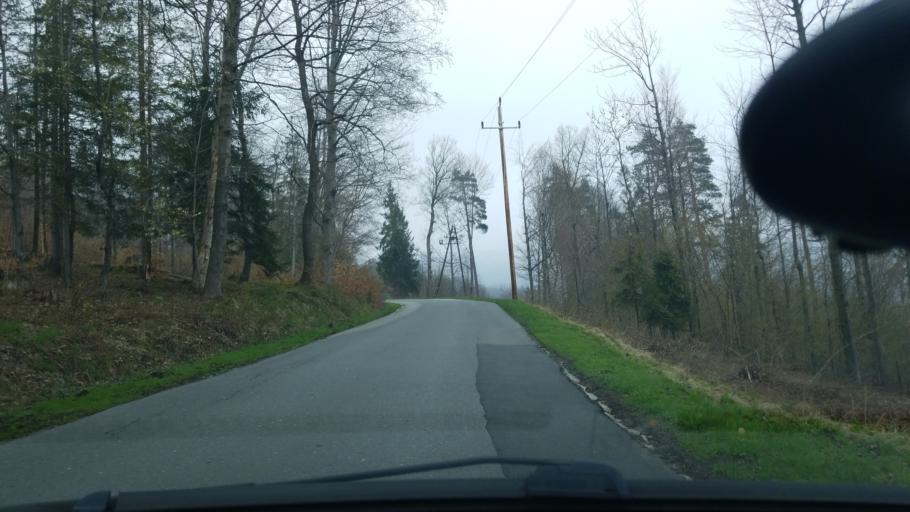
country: PL
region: Silesian Voivodeship
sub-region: Powiat cieszynski
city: Ustron
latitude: 49.7068
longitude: 18.8417
